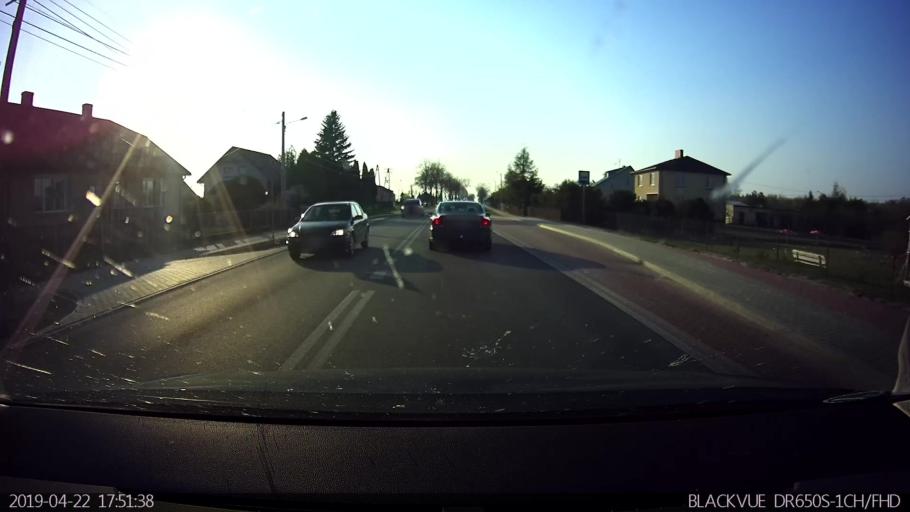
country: PL
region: Masovian Voivodeship
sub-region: Powiat wegrowski
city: Wegrow
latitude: 52.4361
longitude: 21.9914
